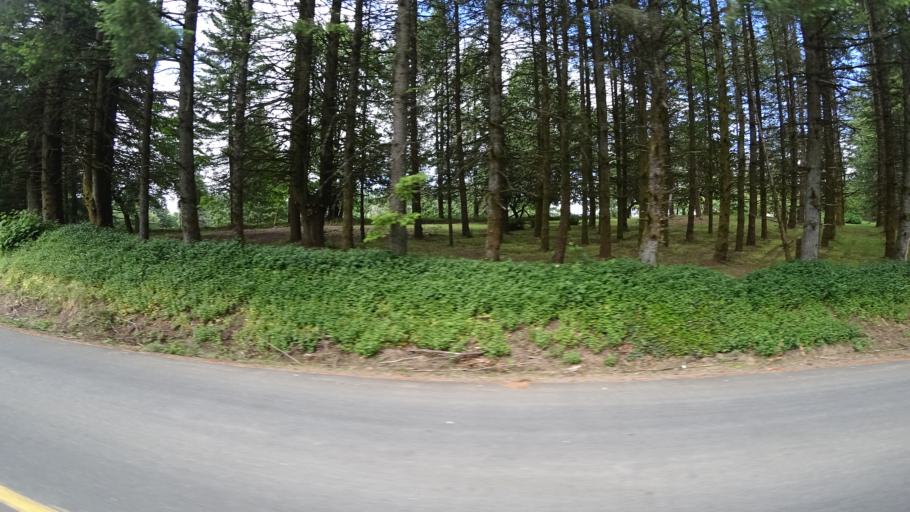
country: US
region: Oregon
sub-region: Washington County
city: Bethany
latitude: 45.6128
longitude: -122.8341
